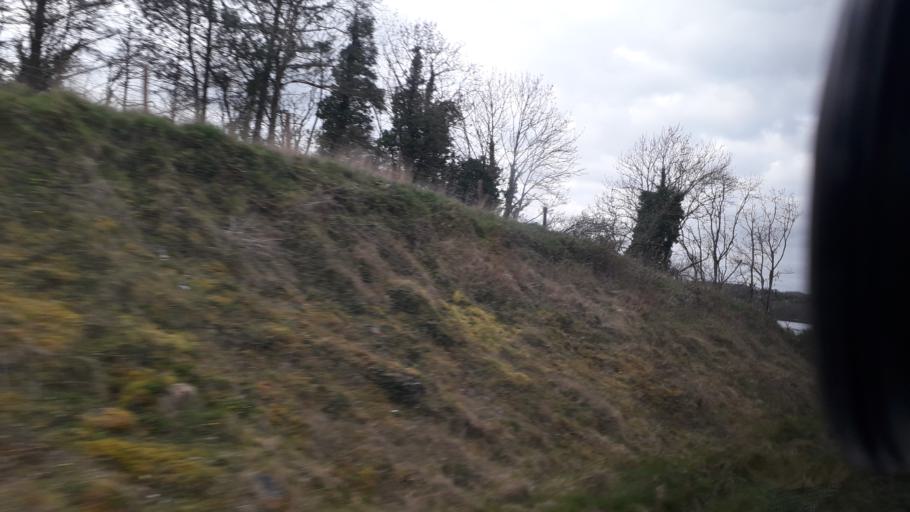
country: IE
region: Leinster
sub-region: An Iarmhi
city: An Muileann gCearr
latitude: 53.5666
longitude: -7.3624
